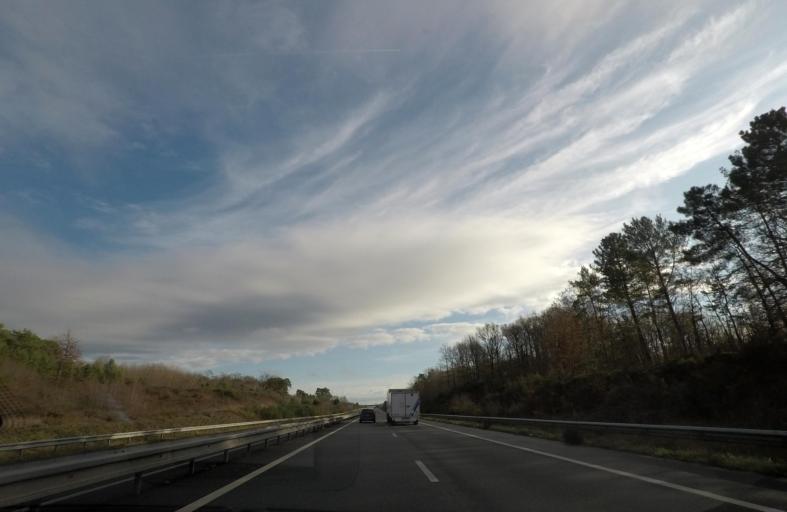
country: FR
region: Centre
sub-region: Departement du Loir-et-Cher
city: Villefranche-sur-Cher
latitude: 47.3142
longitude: 1.8149
